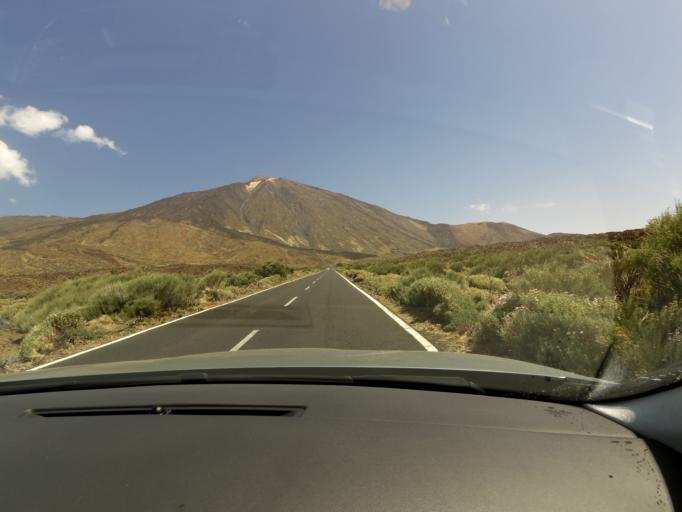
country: ES
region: Canary Islands
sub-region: Provincia de Santa Cruz de Tenerife
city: Vilaflor
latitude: 28.2287
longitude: -16.6289
